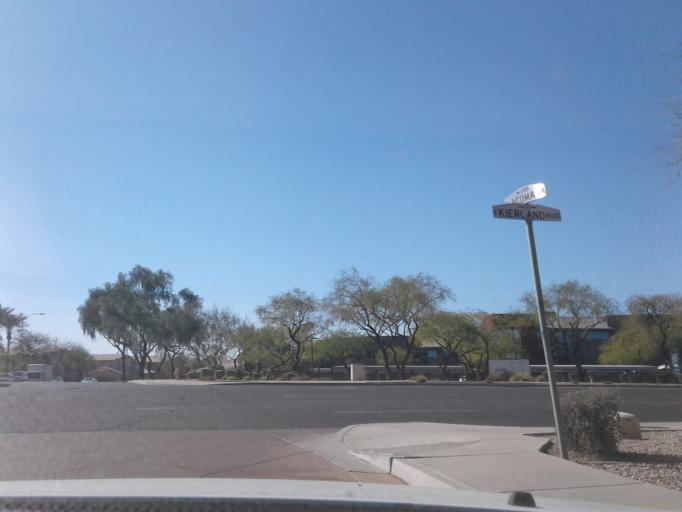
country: US
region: Arizona
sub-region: Maricopa County
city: Paradise Valley
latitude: 33.6192
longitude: -111.9306
